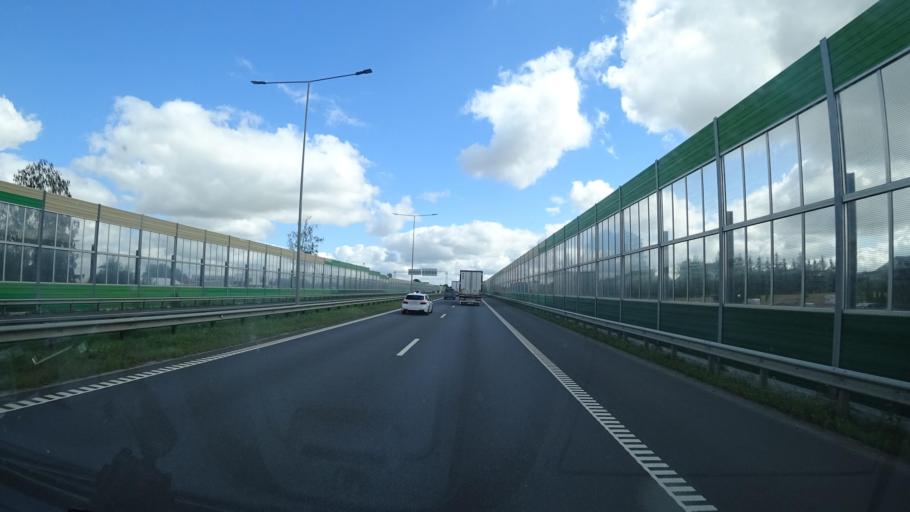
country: LT
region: Marijampoles apskritis
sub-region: Marijampole Municipality
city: Marijampole
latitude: 54.5984
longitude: 23.3973
